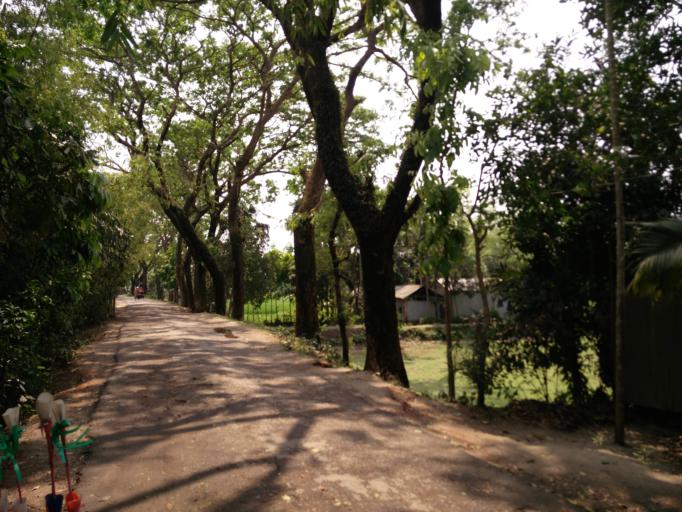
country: BD
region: Dhaka
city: Sherpur
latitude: 24.9417
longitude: 90.1600
